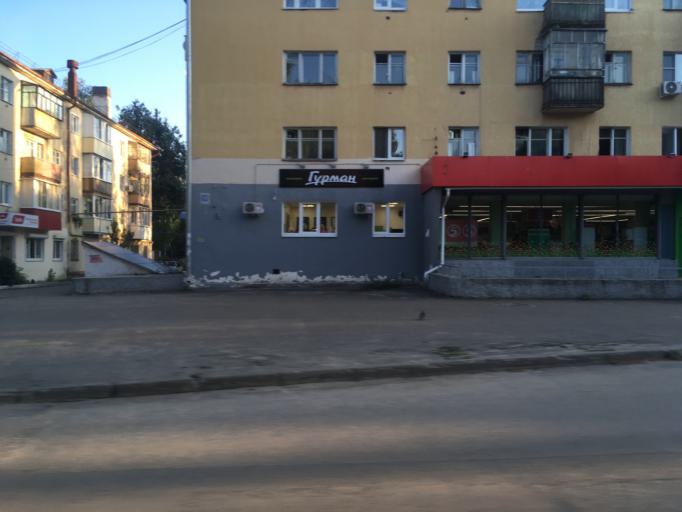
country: RU
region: Mariy-El
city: Yoshkar-Ola
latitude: 56.6472
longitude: 47.8847
